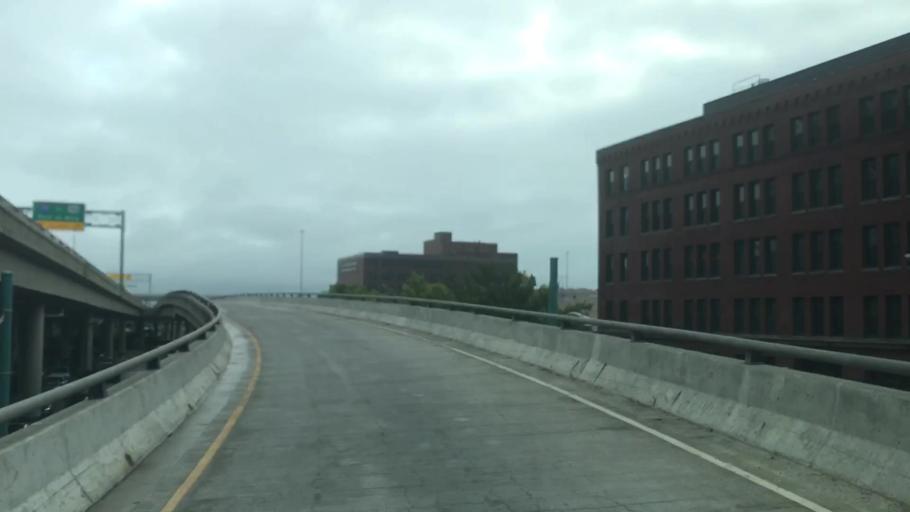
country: US
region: Wisconsin
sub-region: Milwaukee County
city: Milwaukee
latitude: 43.0354
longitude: -87.9064
